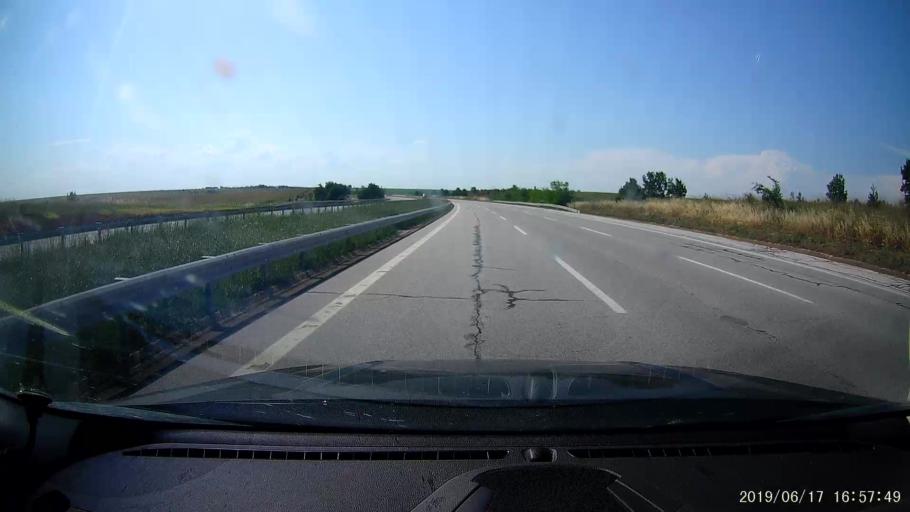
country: TR
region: Edirne
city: Haskoy
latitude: 41.6068
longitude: 26.9053
